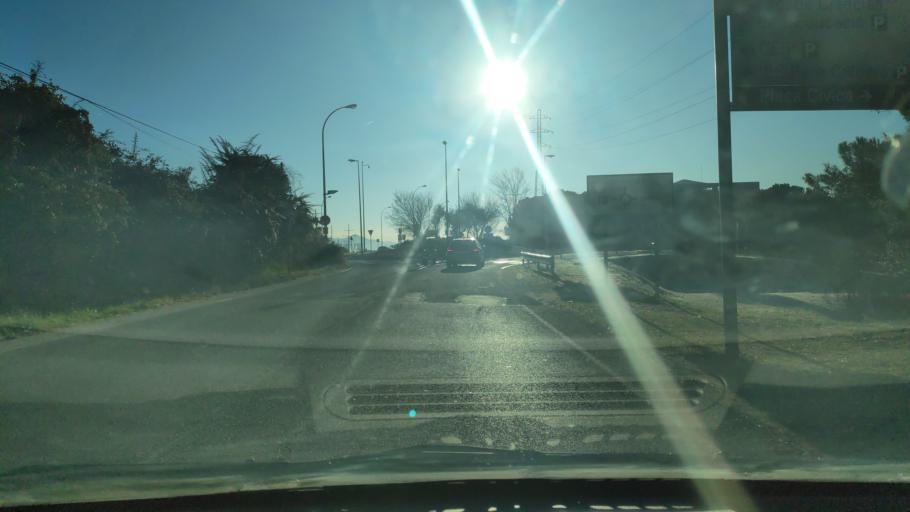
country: ES
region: Catalonia
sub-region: Provincia de Barcelona
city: Barbera del Valles
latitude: 41.5081
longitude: 2.1017
